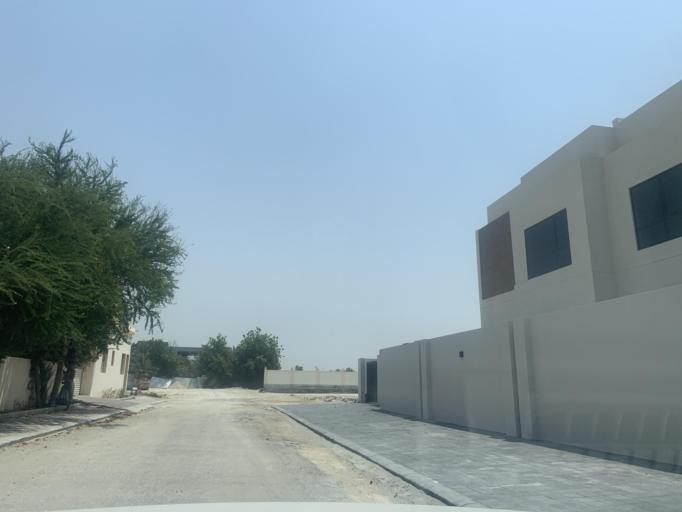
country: BH
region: Central Governorate
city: Madinat Hamad
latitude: 26.1477
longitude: 50.4638
